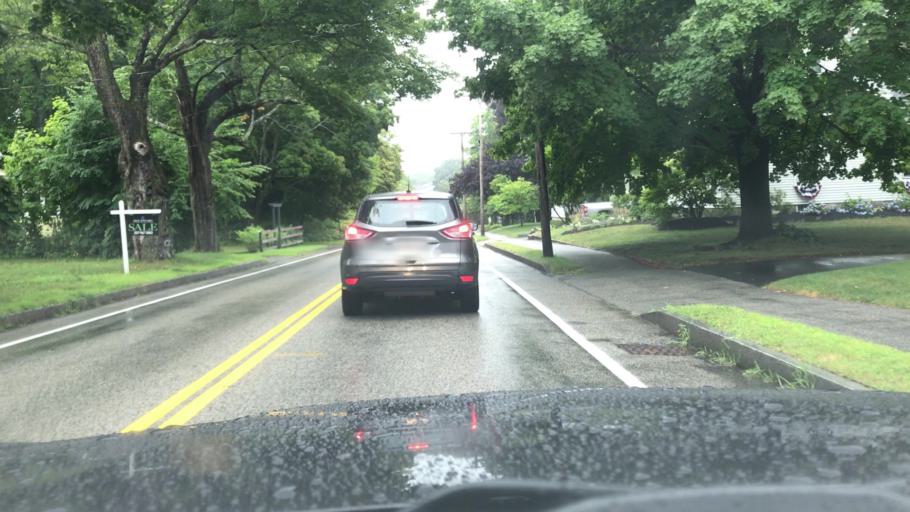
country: US
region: Maine
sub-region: York County
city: Kennebunk
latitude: 43.3888
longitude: -70.5412
